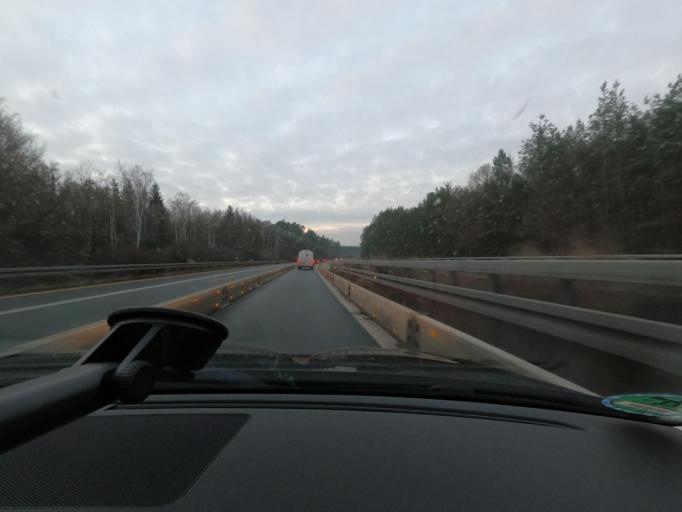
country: DE
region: Bavaria
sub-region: Upper Franconia
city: Strullendorf
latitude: 49.8708
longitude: 10.9501
